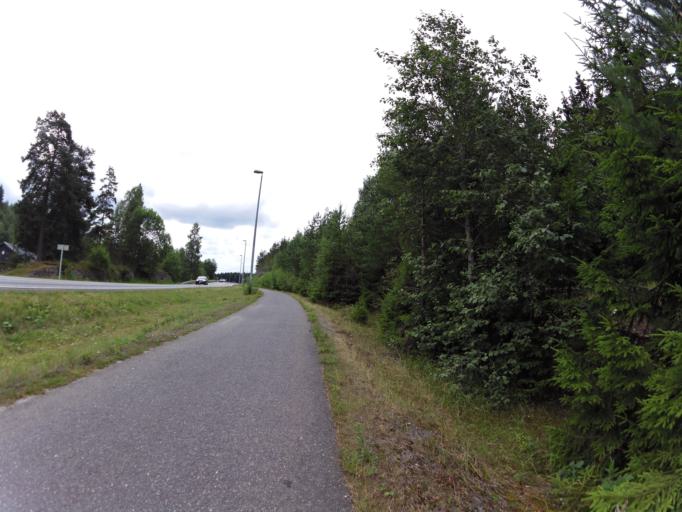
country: NO
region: Akershus
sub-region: Ski
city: Ski
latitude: 59.7455
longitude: 10.7809
